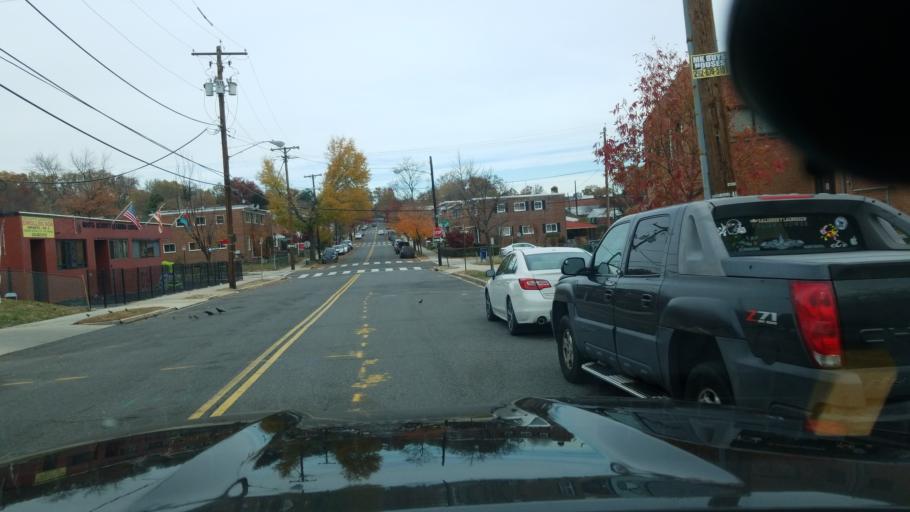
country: US
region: Maryland
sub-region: Montgomery County
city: Takoma Park
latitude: 38.9658
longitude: -77.0090
